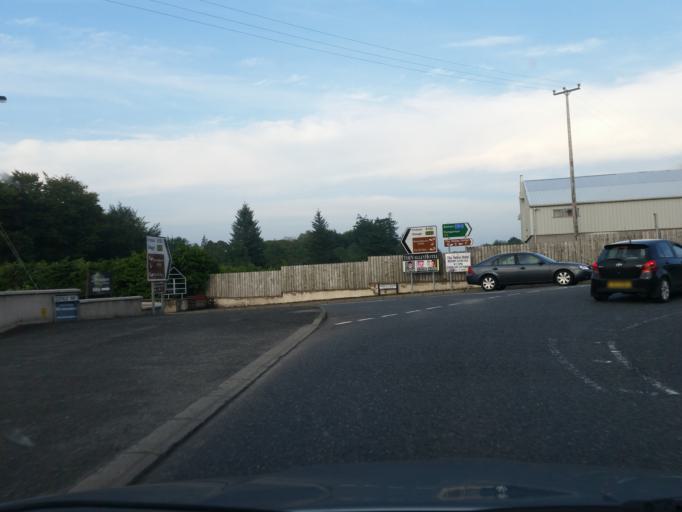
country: GB
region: Northern Ireland
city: Fivemiletown
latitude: 54.3793
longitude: -7.3138
